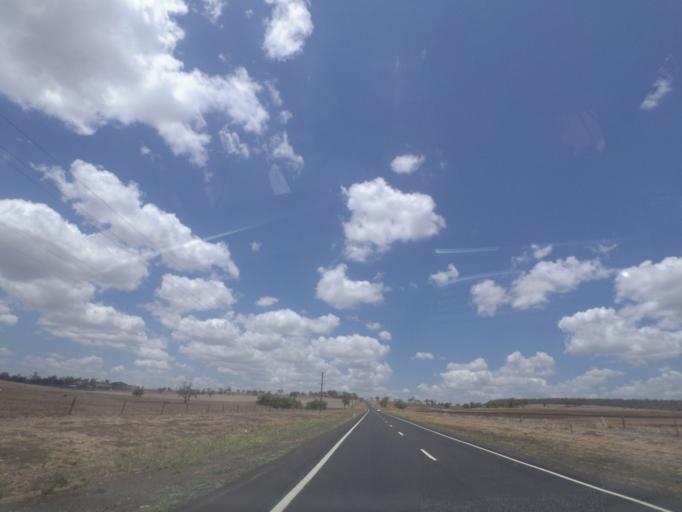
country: AU
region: Queensland
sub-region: Toowoomba
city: Top Camp
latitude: -27.7215
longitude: 151.9116
